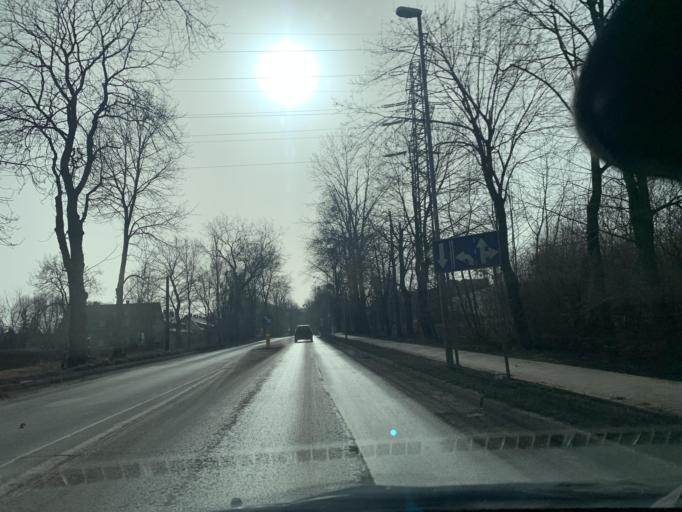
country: PL
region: Silesian Voivodeship
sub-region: Swietochlowice
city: Swietochlowice
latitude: 50.3248
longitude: 18.8915
